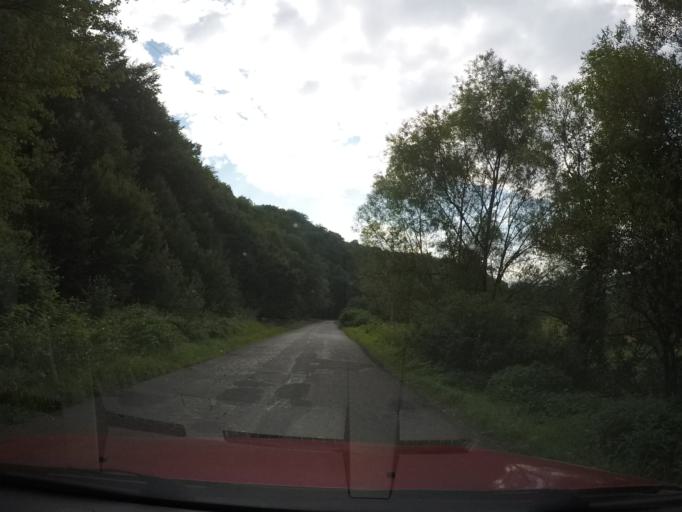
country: UA
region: Zakarpattia
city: Velykyi Bereznyi
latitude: 48.9515
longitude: 22.5569
